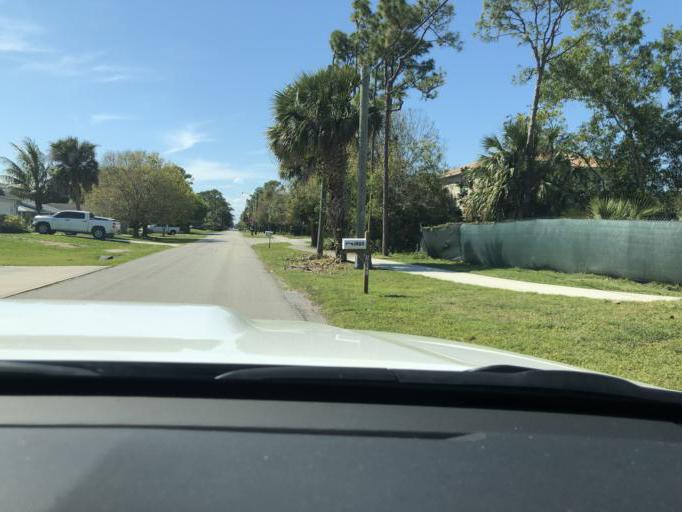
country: US
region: Florida
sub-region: Martin County
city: Palm City
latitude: 27.1684
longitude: -80.2732
